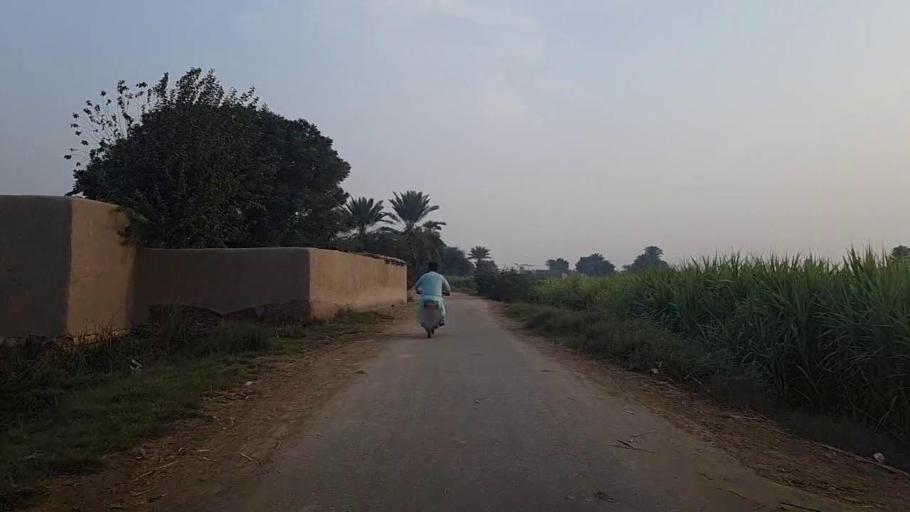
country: PK
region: Sindh
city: Kot Diji
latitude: 27.3805
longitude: 68.6641
